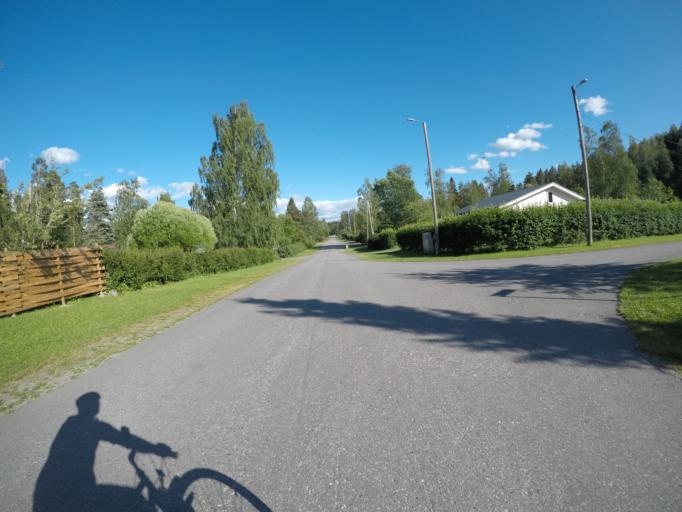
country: FI
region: Haeme
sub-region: Haemeenlinna
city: Haemeenlinna
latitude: 61.0177
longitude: 24.4909
